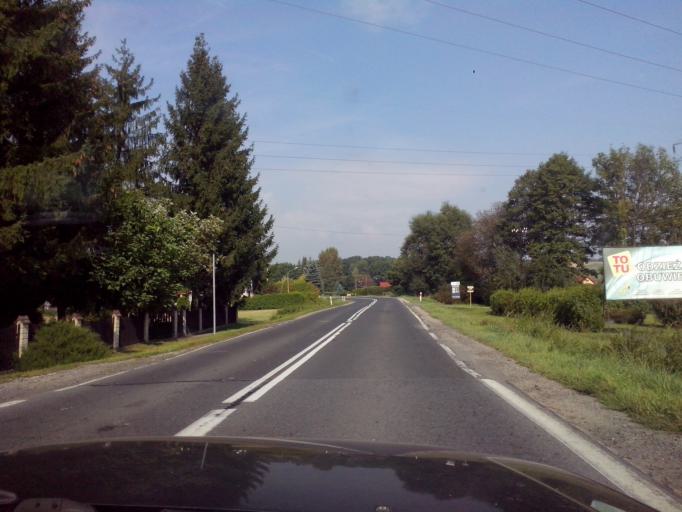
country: PL
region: Subcarpathian Voivodeship
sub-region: Powiat strzyzowski
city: Czudec
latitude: 49.9366
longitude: 21.8163
